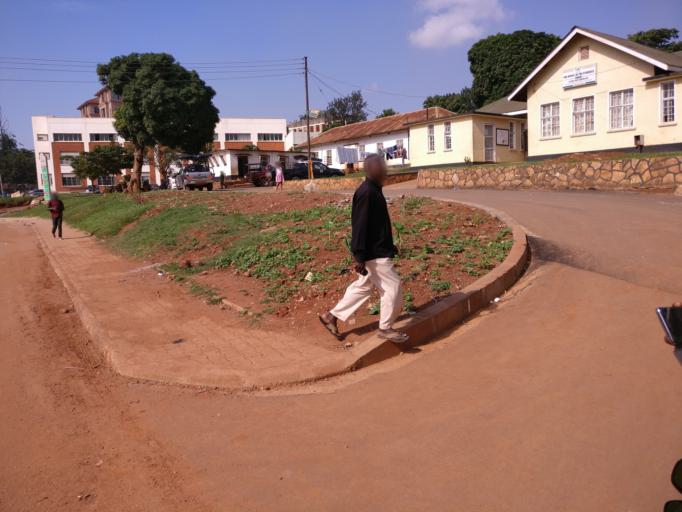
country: UG
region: Central Region
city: Kampala Central Division
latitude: 0.3357
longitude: 32.5710
